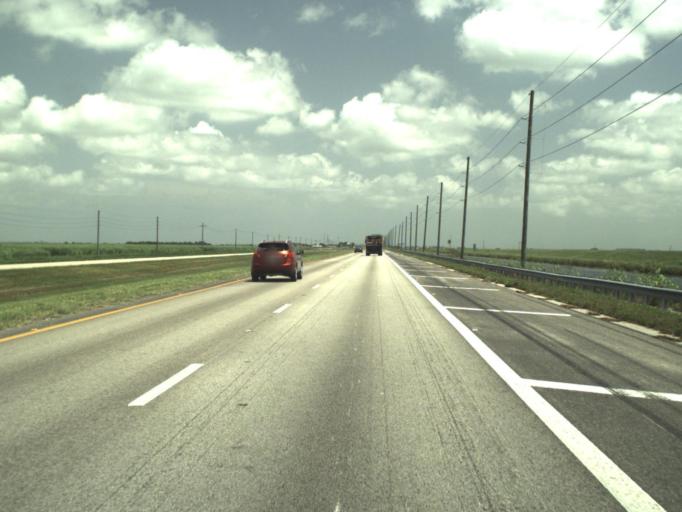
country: US
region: Florida
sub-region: Palm Beach County
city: Belle Glade Camp
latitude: 26.5987
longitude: -80.7112
